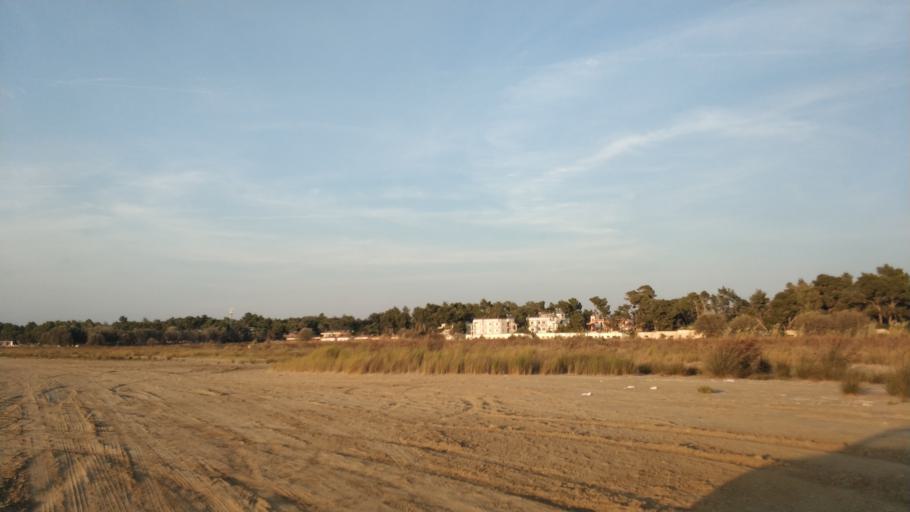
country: AL
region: Fier
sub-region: Rrethi i Lushnjes
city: Divjake
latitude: 40.9691
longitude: 19.4760
